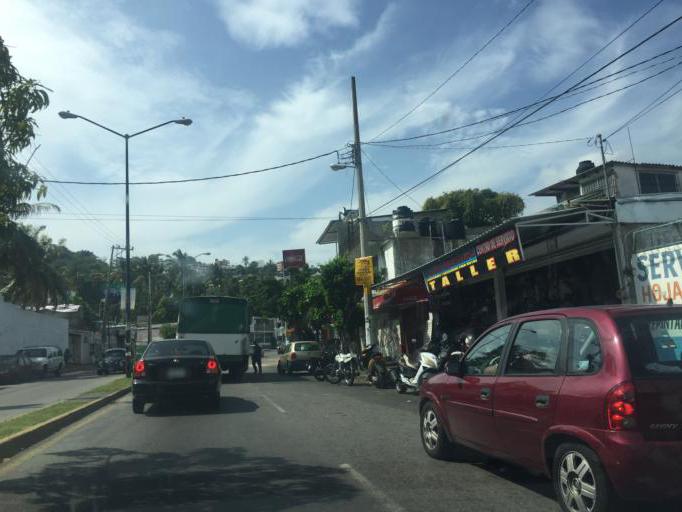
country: MX
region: Guerrero
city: Acapulco de Juarez
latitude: 16.8566
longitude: -99.9137
